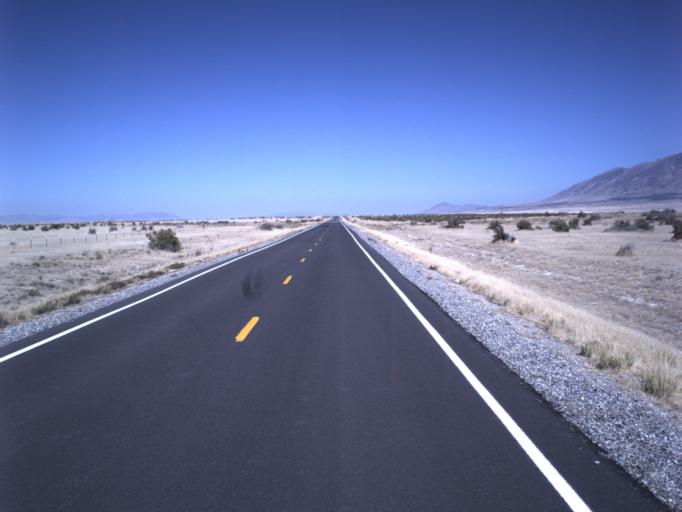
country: US
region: Utah
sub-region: Tooele County
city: Grantsville
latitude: 40.2747
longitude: -112.7415
